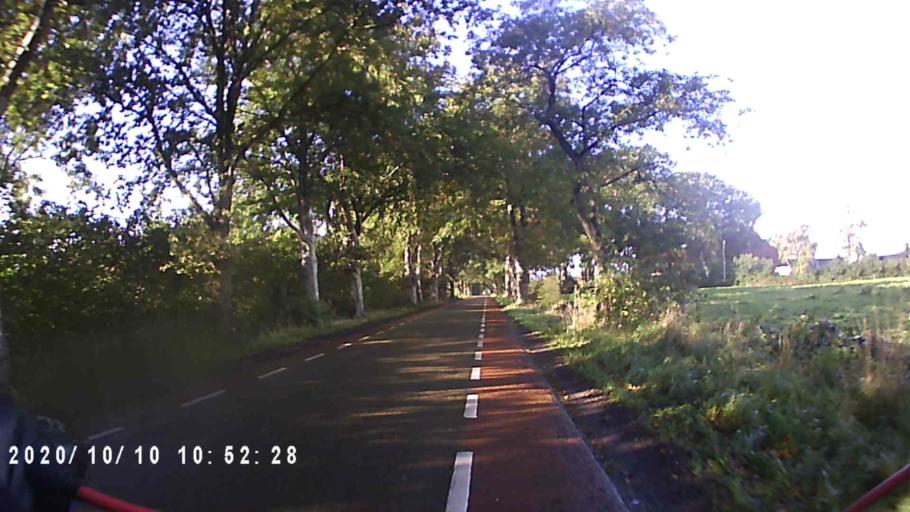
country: NL
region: Friesland
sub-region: Gemeente Achtkarspelen
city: Surhuisterveen
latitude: 53.1580
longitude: 6.2231
